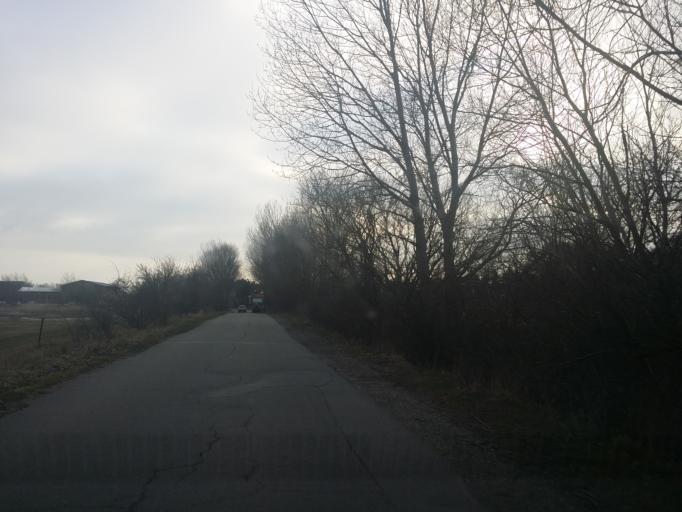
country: DE
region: Schleswig-Holstein
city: Heiligenhafen
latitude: 54.4524
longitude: 11.0109
